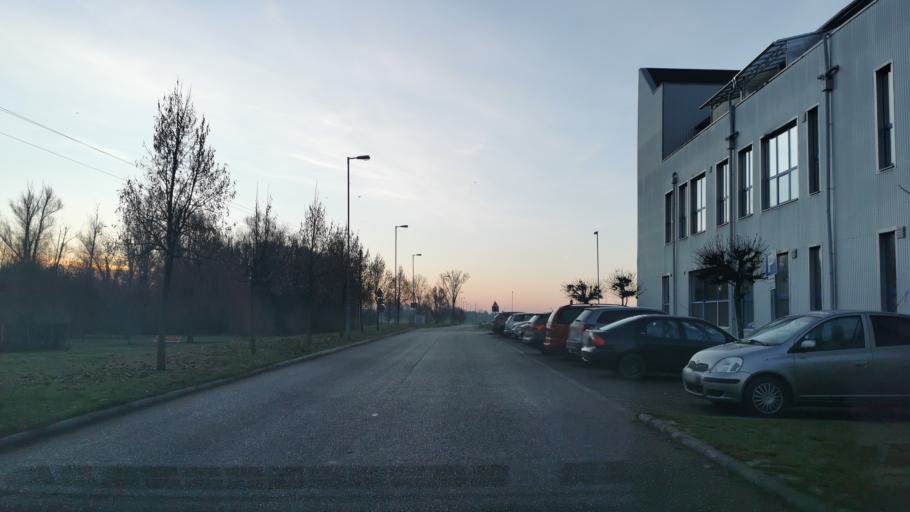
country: HU
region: Hajdu-Bihar
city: Debrecen
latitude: 47.5977
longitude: 21.5793
